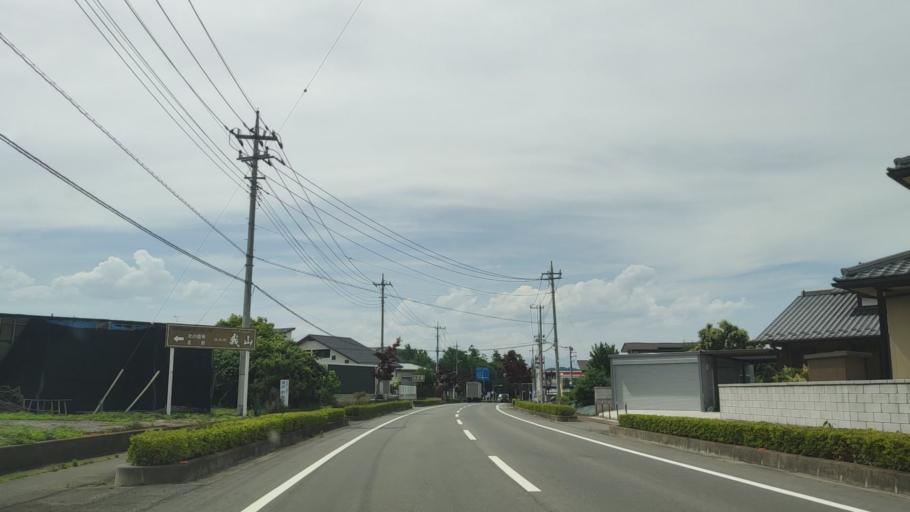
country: JP
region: Gunma
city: Tomioka
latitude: 36.2489
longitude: 138.8837
